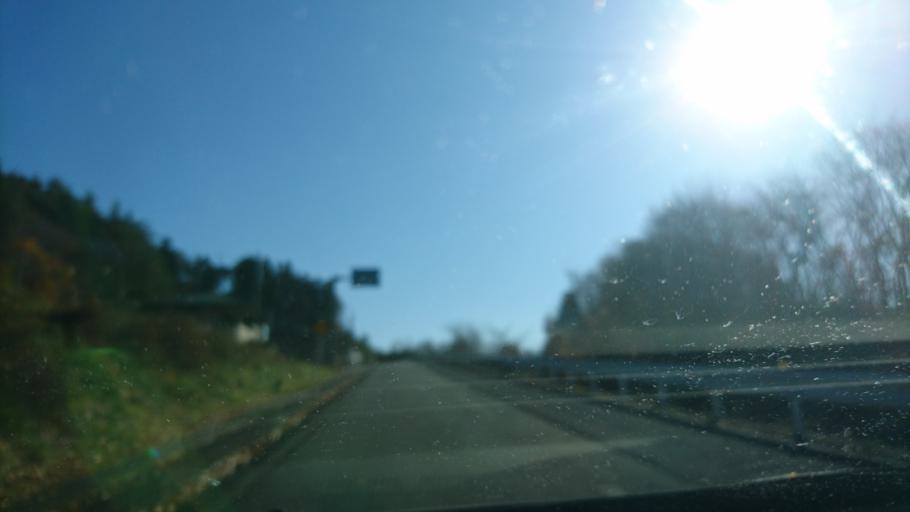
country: JP
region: Iwate
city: Ichinoseki
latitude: 38.9986
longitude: 141.2696
